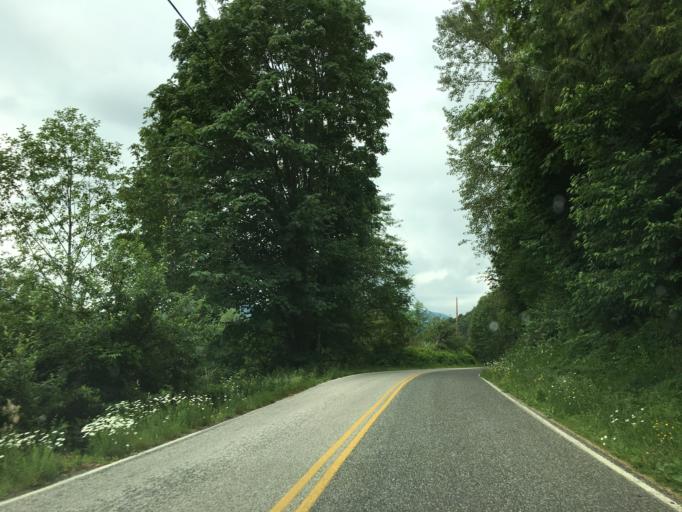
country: US
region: Washington
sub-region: Whatcom County
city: Peaceful Valley
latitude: 48.9956
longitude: -122.0692
